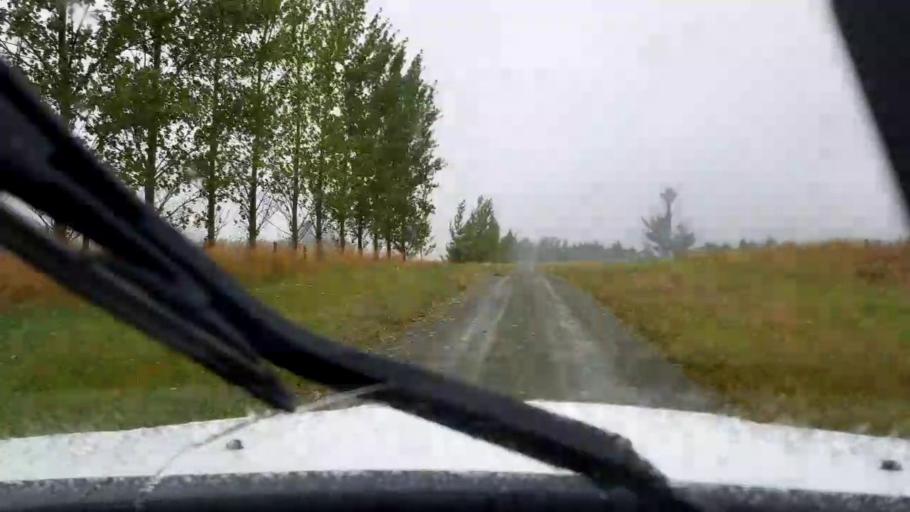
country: NZ
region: Canterbury
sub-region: Timaru District
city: Pleasant Point
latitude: -44.1993
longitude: 171.0905
